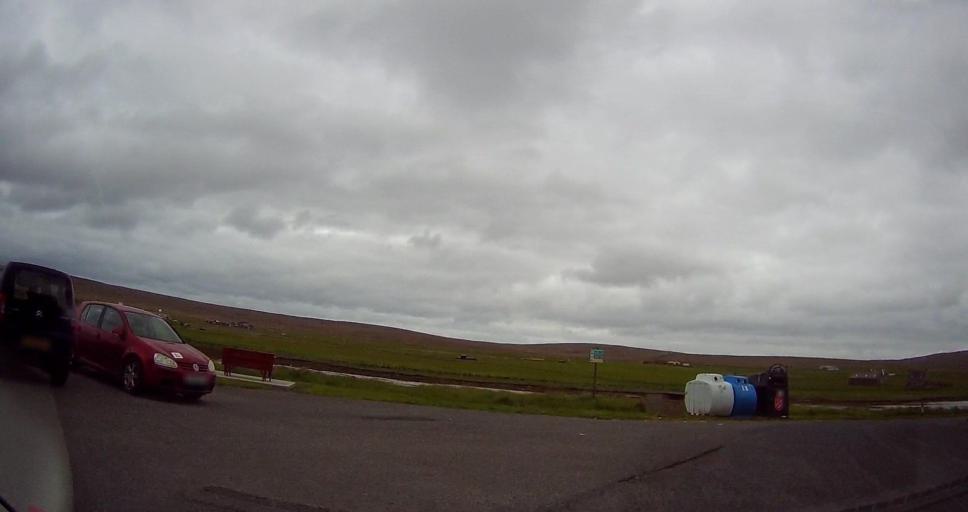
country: GB
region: Scotland
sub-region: Shetland Islands
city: Shetland
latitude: 60.7573
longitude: -0.8602
